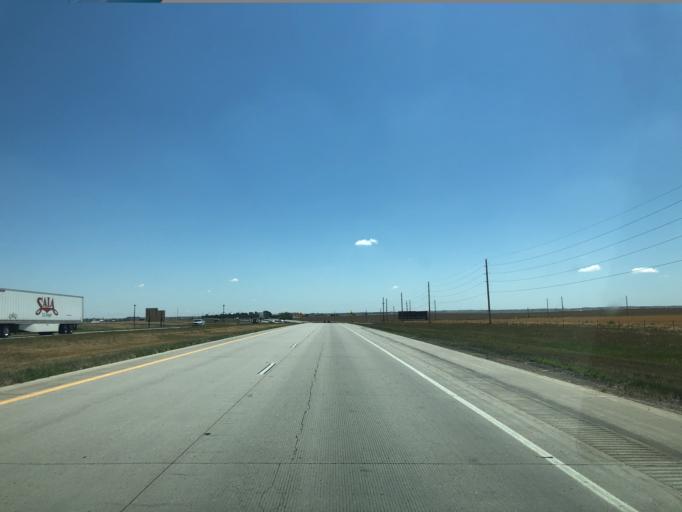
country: US
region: Colorado
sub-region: Adams County
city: Aurora
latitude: 39.7386
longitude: -104.6451
